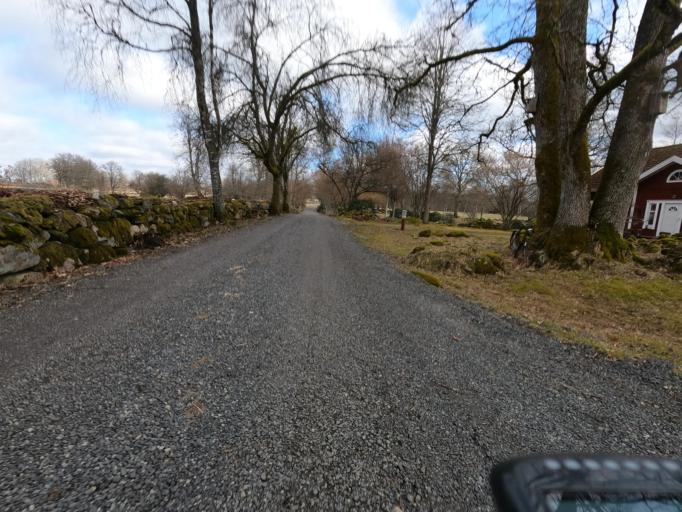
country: SE
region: Kronoberg
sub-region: Alvesta Kommun
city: Vislanda
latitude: 56.8170
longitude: 14.3679
